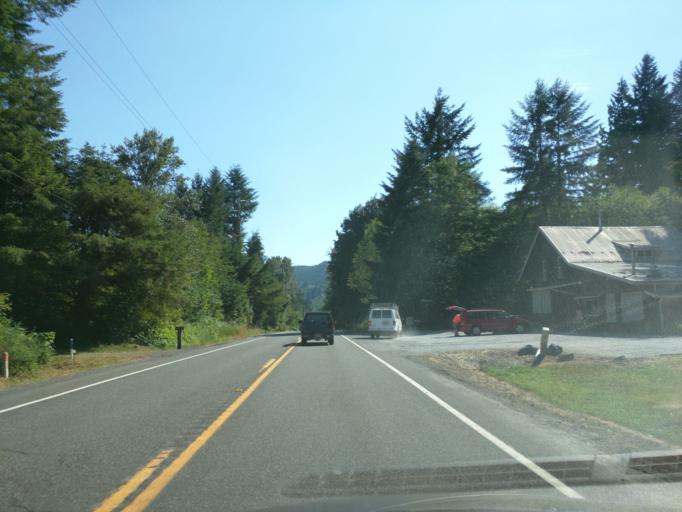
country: US
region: Washington
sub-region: Whatcom County
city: Peaceful Valley
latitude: 48.8909
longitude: -122.1510
